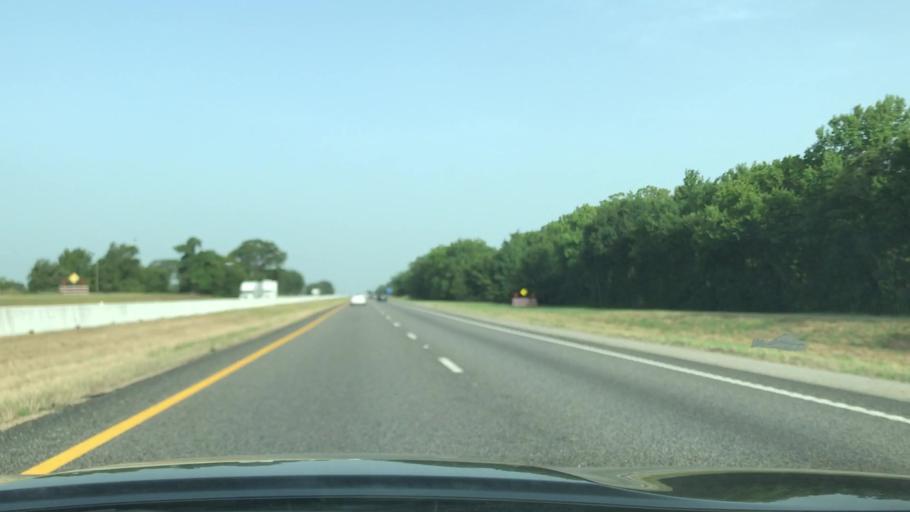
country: US
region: Texas
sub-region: Van Zandt County
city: Van
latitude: 32.5099
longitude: -95.6607
